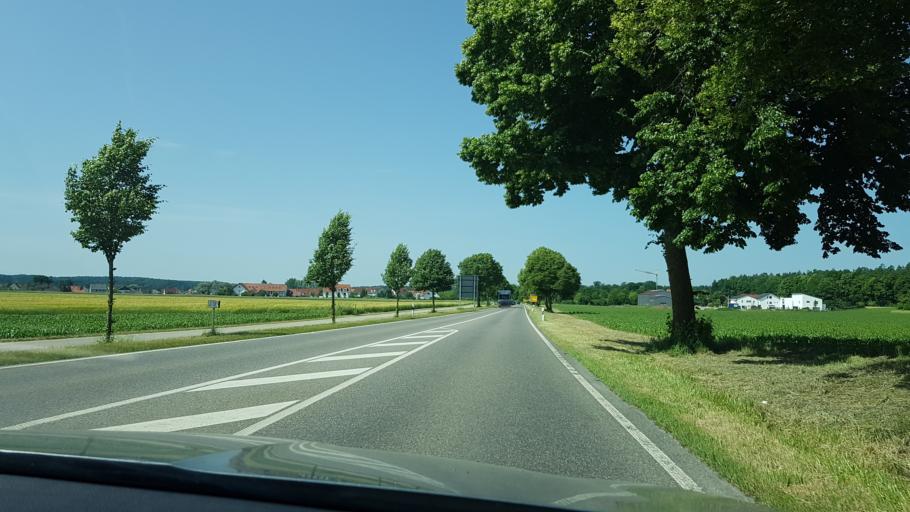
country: DE
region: Bavaria
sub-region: Upper Bavaria
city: Schongeising
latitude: 48.1480
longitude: 11.2089
